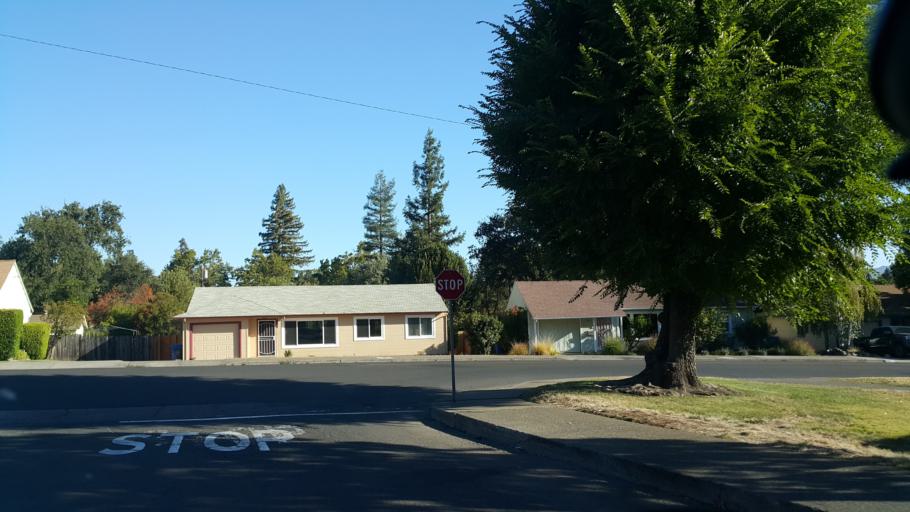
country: US
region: California
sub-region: Mendocino County
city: Ukiah
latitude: 39.1401
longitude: -123.2147
